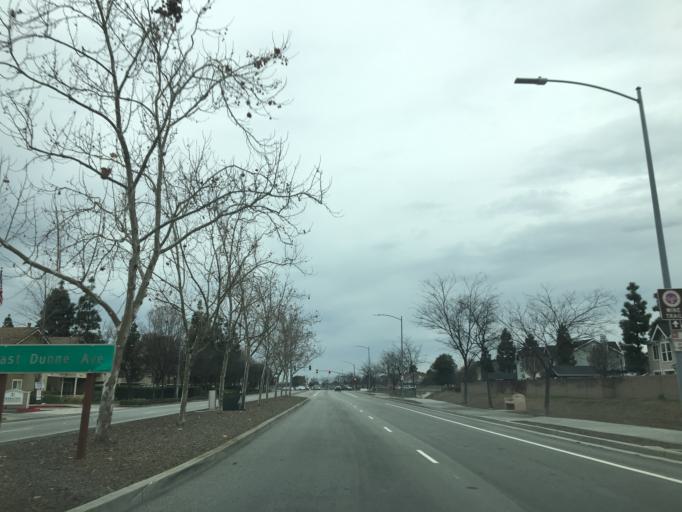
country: US
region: California
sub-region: Santa Clara County
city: Morgan Hill
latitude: 37.1256
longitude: -121.6436
